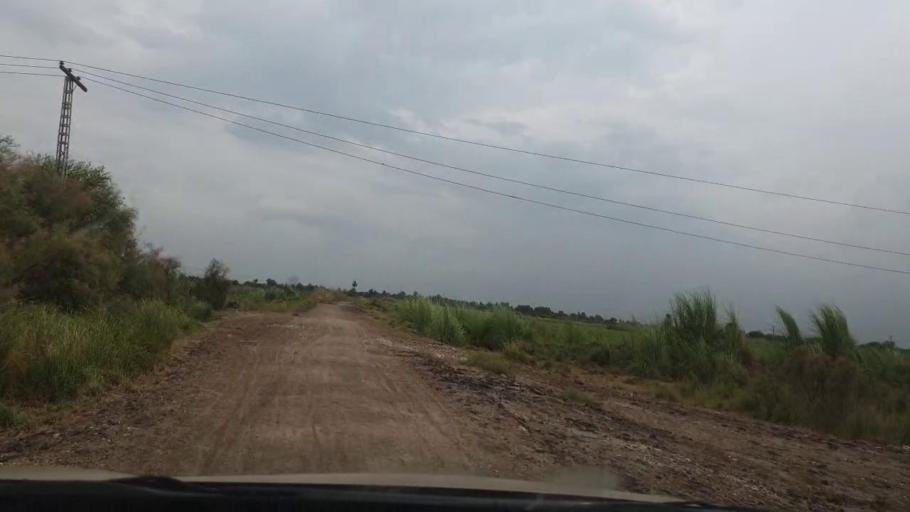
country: PK
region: Sindh
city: Ratodero
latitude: 27.8027
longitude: 68.3136
